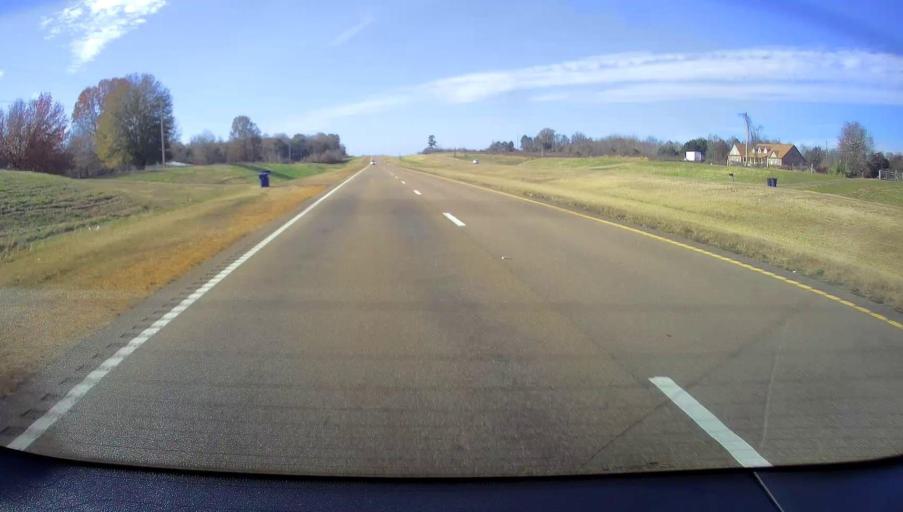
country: US
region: Mississippi
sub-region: Benton County
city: Ashland
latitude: 34.9457
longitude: -89.1752
